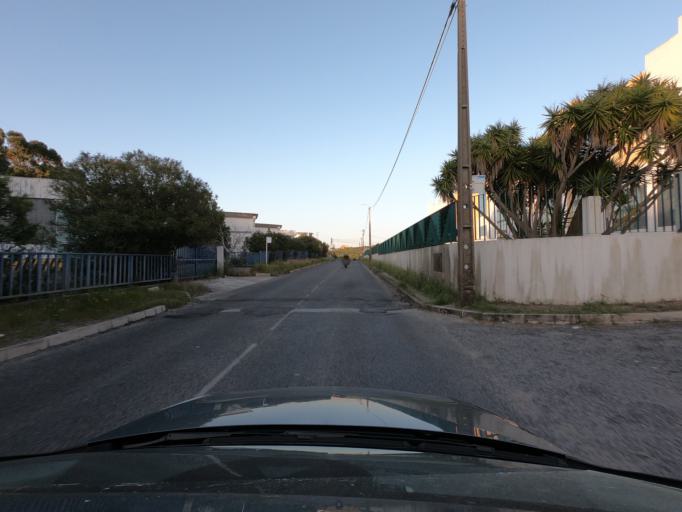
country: PT
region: Lisbon
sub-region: Sintra
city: Sintra
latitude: 38.7607
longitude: -9.3675
